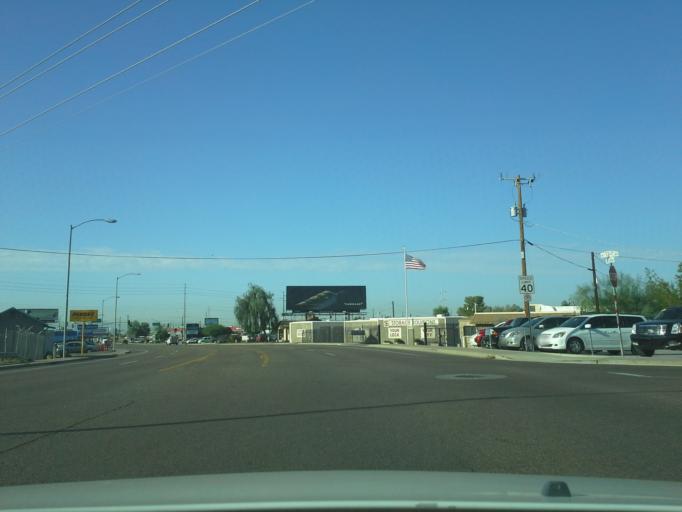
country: US
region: Arizona
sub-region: Maricopa County
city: Paradise Valley
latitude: 33.5766
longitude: -112.0564
